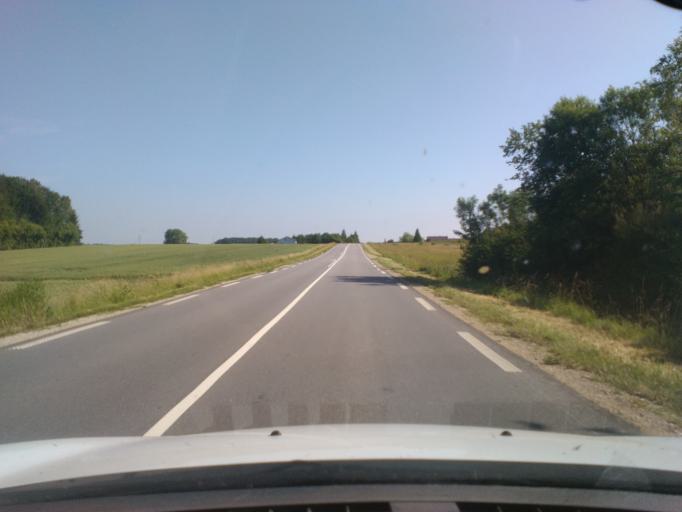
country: FR
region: Lorraine
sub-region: Departement des Vosges
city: Aydoilles
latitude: 48.2363
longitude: 6.5983
